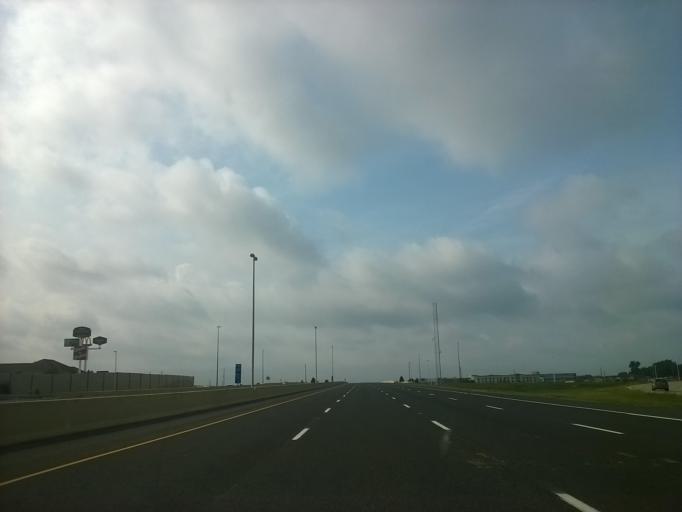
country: US
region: Indiana
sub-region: Boone County
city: Zionsville
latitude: 39.8855
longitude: -86.2694
